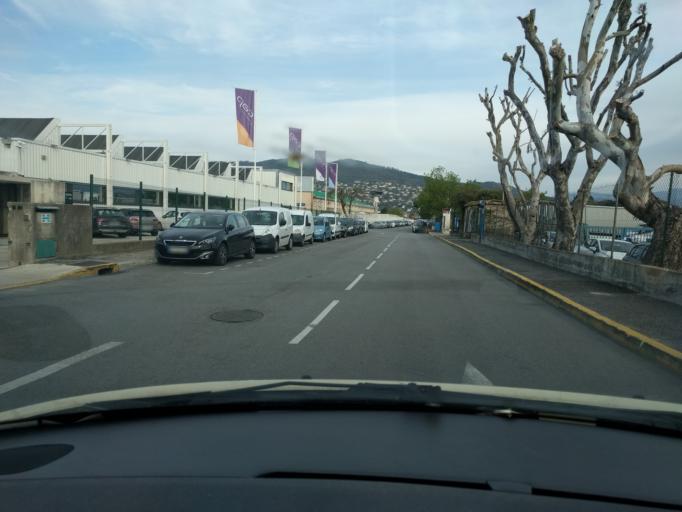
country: FR
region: Provence-Alpes-Cote d'Azur
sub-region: Departement des Alpes-Maritimes
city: Mandelieu-la-Napoule
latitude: 43.5437
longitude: 6.9588
